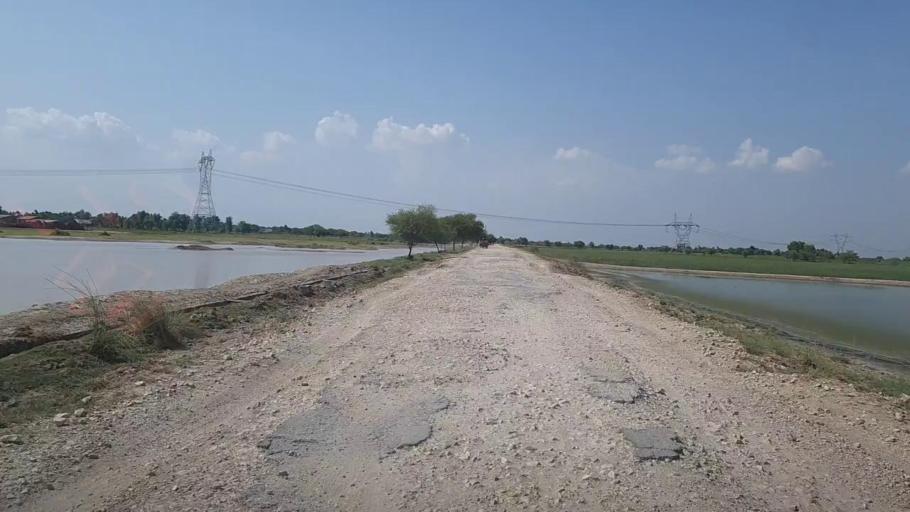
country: PK
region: Sindh
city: Khairpur
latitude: 28.1058
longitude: 69.6230
